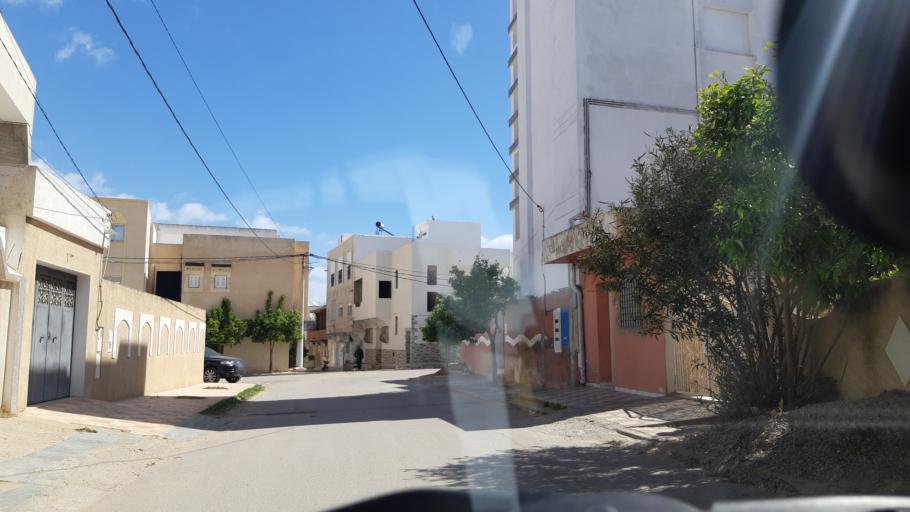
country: TN
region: Susah
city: Akouda
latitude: 35.8909
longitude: 10.5326
